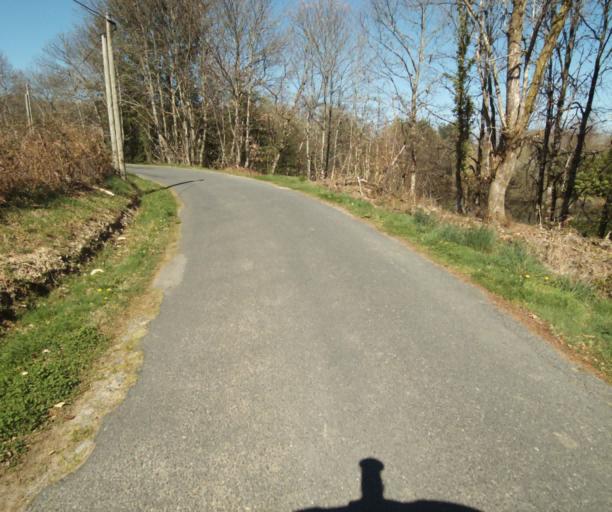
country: FR
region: Limousin
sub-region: Departement de la Correze
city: Saint-Mexant
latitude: 45.2903
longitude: 1.7006
